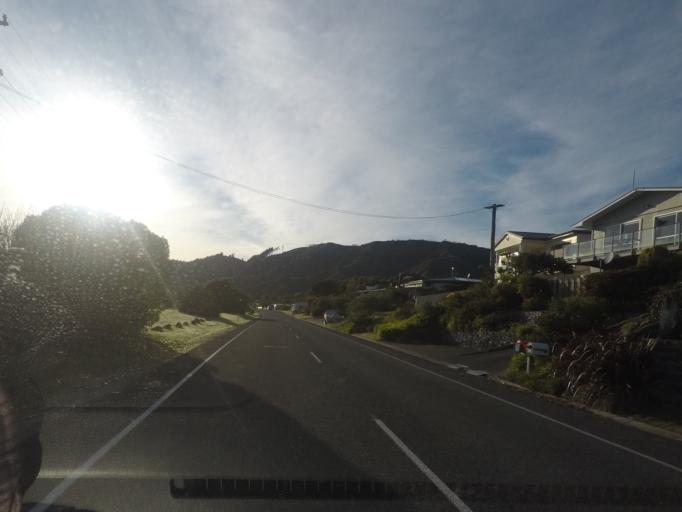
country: NZ
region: Tasman
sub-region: Tasman District
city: Takaka
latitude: -40.8232
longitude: 172.9063
